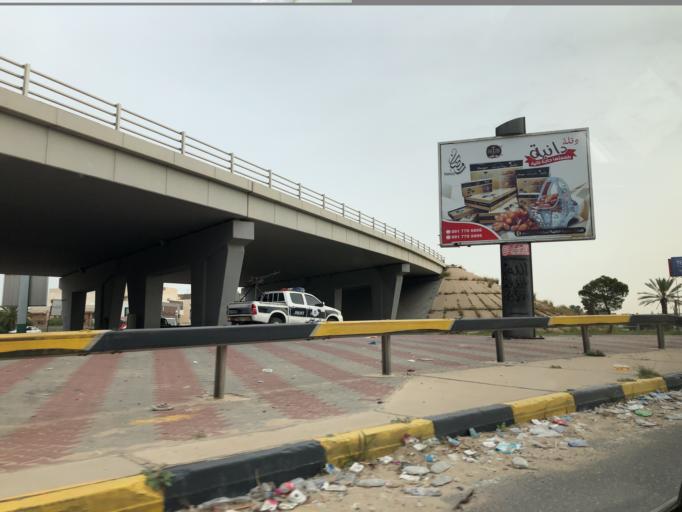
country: LY
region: Tripoli
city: Tripoli
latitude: 32.8681
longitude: 13.1355
